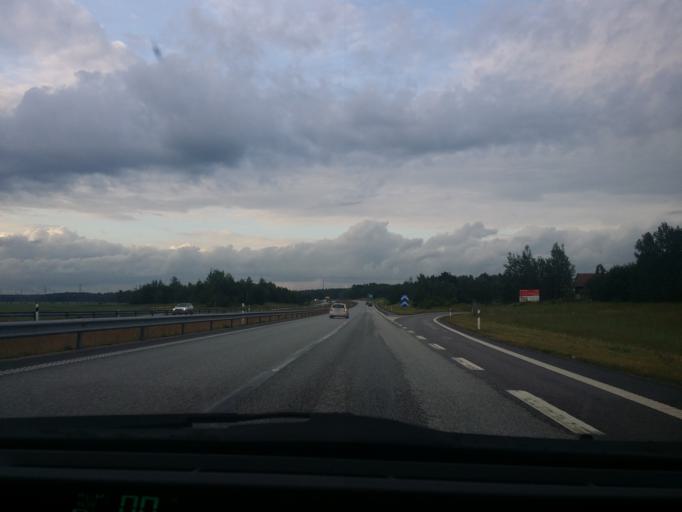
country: SE
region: Vaestmanland
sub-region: Kopings Kommun
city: Koping
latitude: 59.4977
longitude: 15.9288
